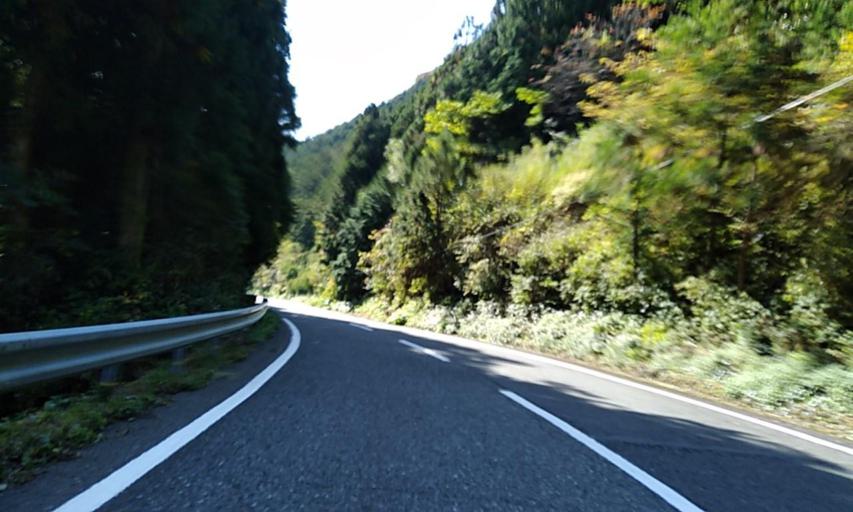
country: JP
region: Wakayama
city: Iwade
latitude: 34.1102
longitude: 135.3449
